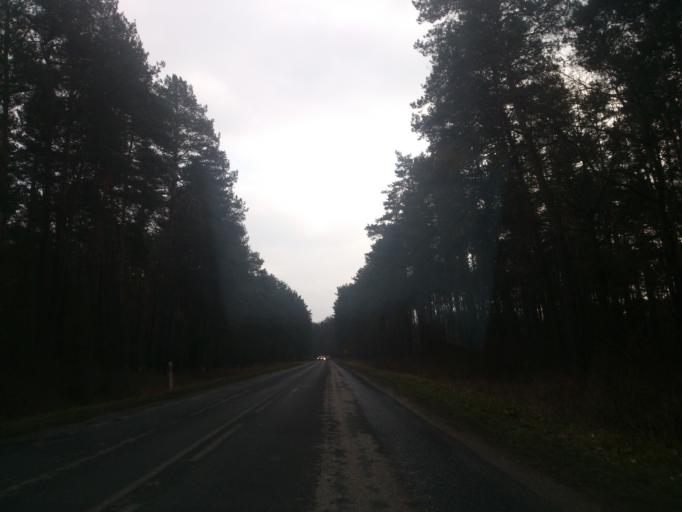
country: PL
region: Kujawsko-Pomorskie
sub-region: Powiat golubsko-dobrzynski
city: Golub-Dobrzyn
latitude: 53.0859
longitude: 19.0550
